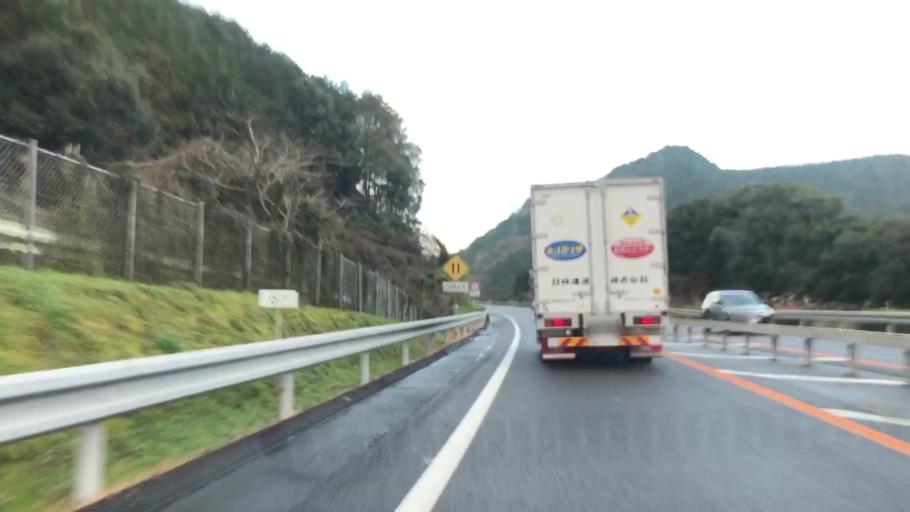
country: JP
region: Saga Prefecture
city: Ureshinomachi-shimojuku
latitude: 33.1563
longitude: 129.9227
